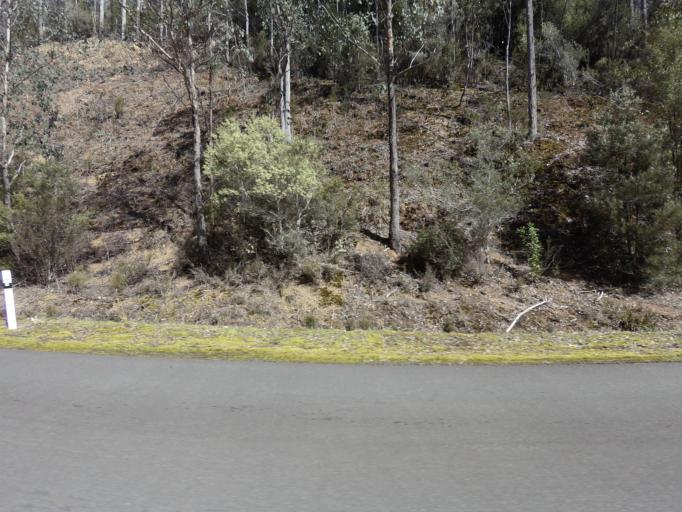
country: AU
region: Tasmania
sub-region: Derwent Valley
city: New Norfolk
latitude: -42.7389
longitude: 146.4960
